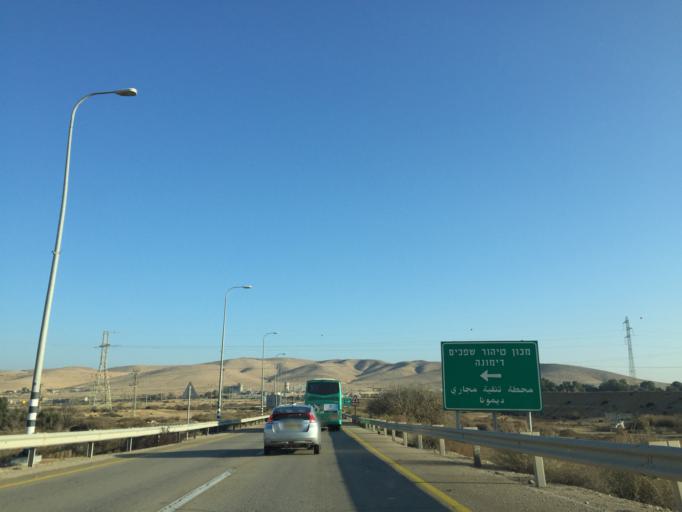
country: IL
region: Southern District
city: Dimona
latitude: 31.0637
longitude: 35.0038
